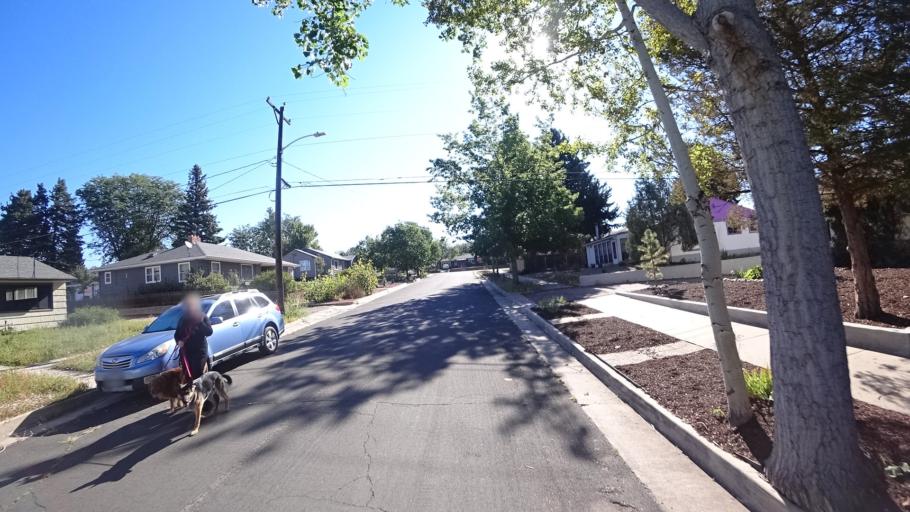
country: US
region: Colorado
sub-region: El Paso County
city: Colorado Springs
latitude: 38.8486
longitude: -104.8009
